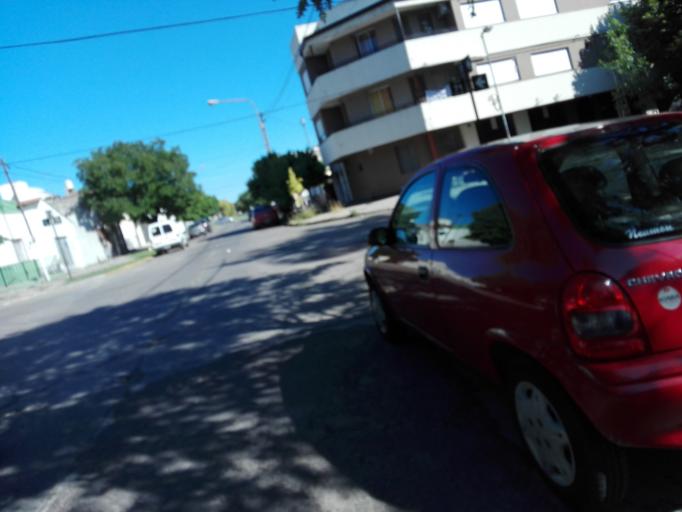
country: AR
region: Buenos Aires
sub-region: Partido de La Plata
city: La Plata
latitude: -34.9488
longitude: -57.9500
